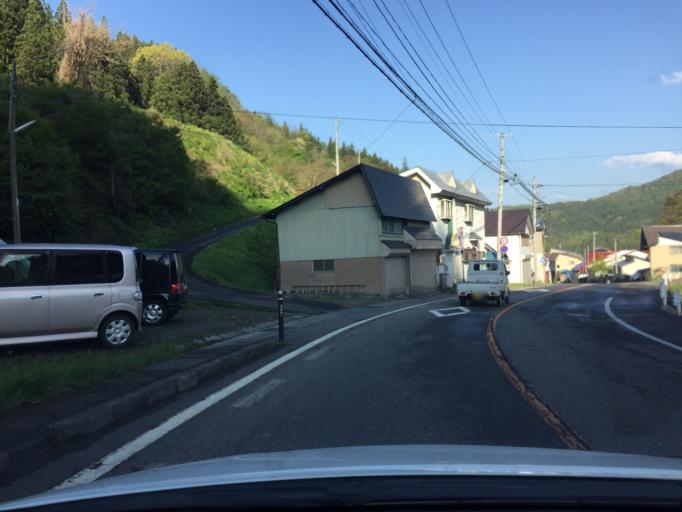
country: JP
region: Fukushima
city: Kitakata
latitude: 37.6677
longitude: 139.9817
